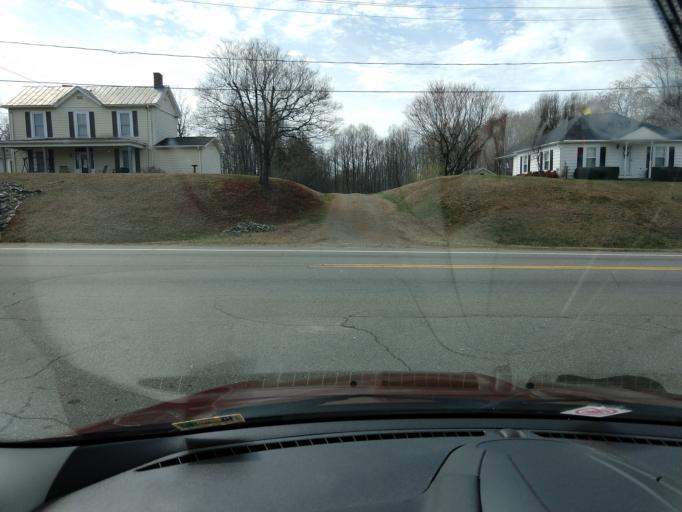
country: US
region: Virginia
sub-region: Henry County
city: Chatmoss
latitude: 36.5760
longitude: -79.8556
